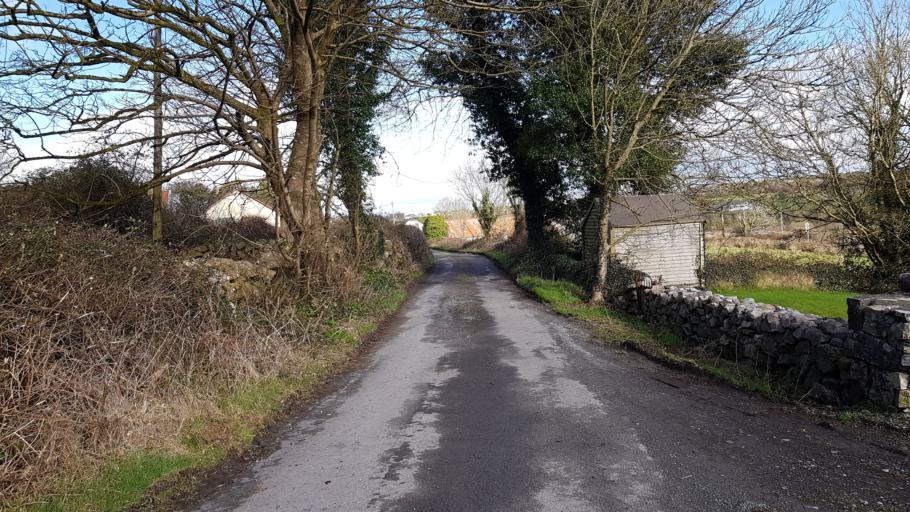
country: IE
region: Connaught
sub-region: County Galway
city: Gaillimh
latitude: 53.3096
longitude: -9.0280
